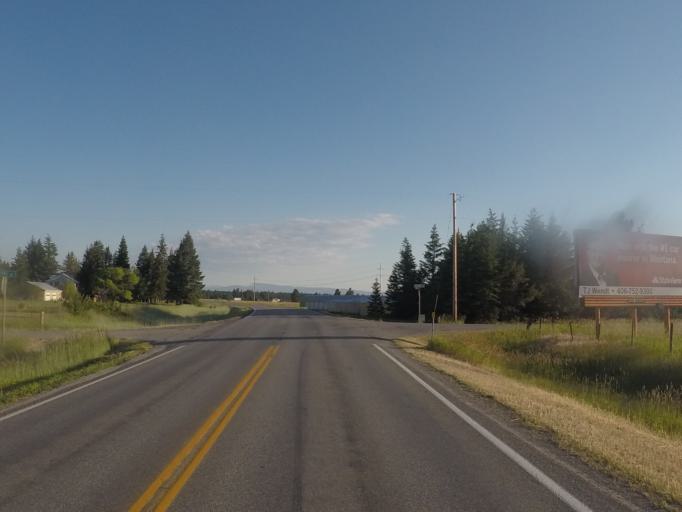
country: US
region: Montana
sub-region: Flathead County
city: Columbia Falls
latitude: 48.3567
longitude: -114.1580
